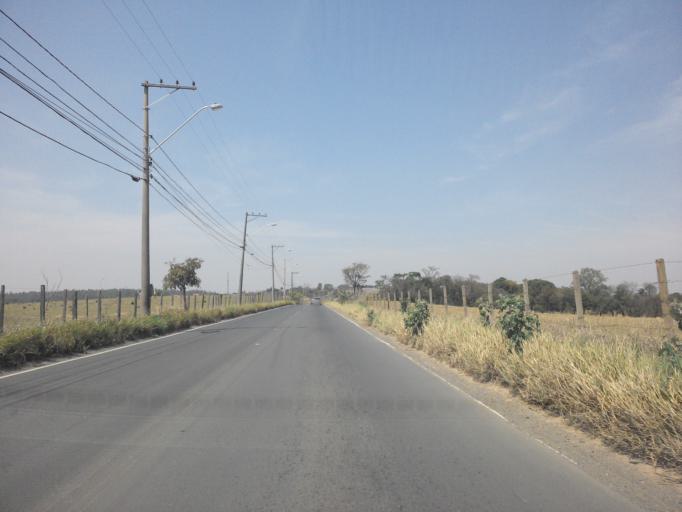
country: BR
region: Sao Paulo
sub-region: Hortolandia
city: Hortolandia
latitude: -22.9227
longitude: -47.1902
